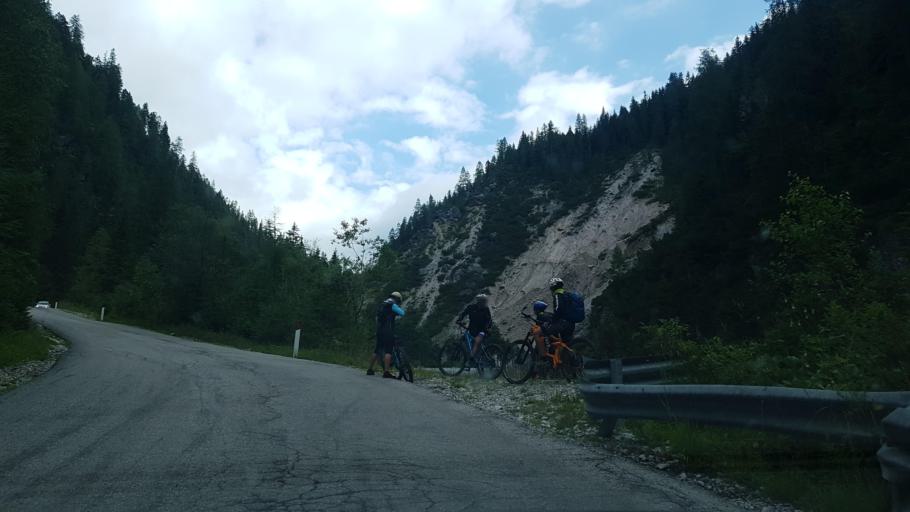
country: IT
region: Veneto
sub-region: Provincia di Belluno
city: San Pietro di Cadore
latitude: 46.5942
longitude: 12.6313
